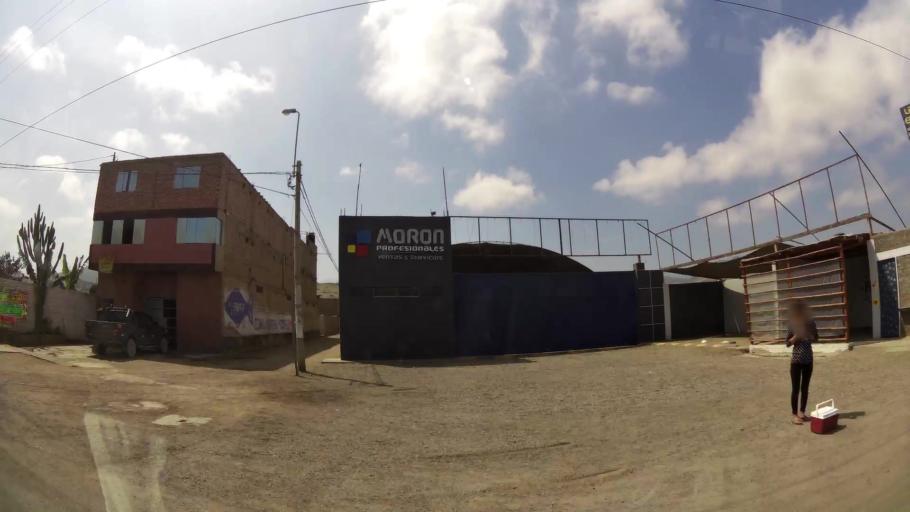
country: PE
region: Lima
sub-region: Provincia de Canete
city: Mala
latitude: -12.6684
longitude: -76.6310
